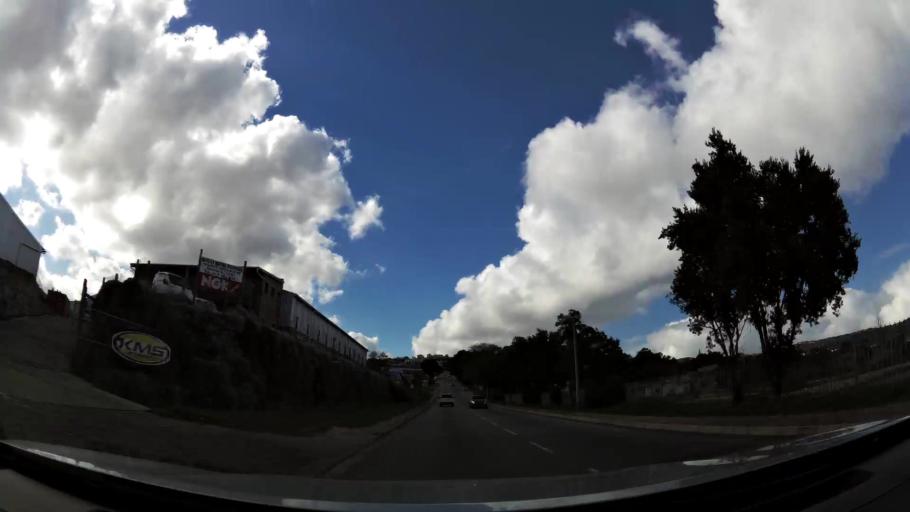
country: ZA
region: Western Cape
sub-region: Eden District Municipality
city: Knysna
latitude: -34.0471
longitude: 23.0737
